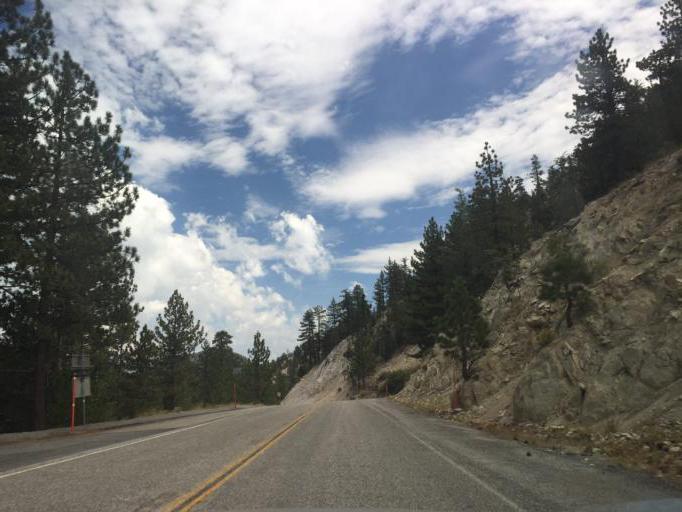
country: US
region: California
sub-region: Los Angeles County
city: Littlerock
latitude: 34.3513
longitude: -117.9343
